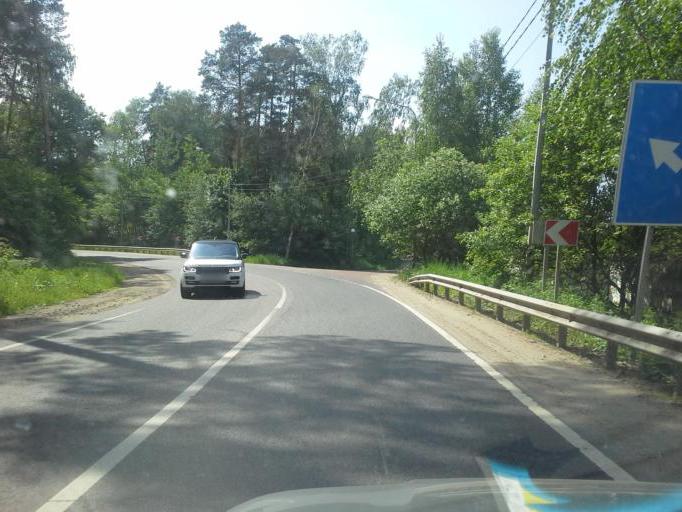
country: RU
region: Moskovskaya
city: Gorki Vtoryye
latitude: 55.7138
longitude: 37.1677
